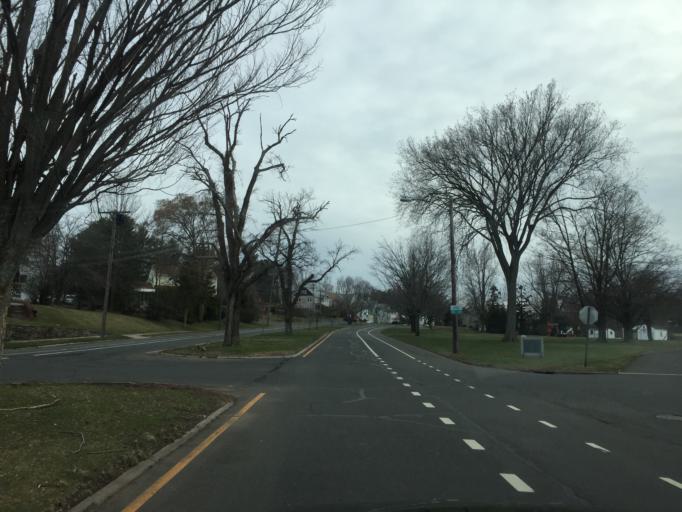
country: US
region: Connecticut
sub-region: Hartford County
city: New Britain
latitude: 41.6871
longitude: -72.7835
